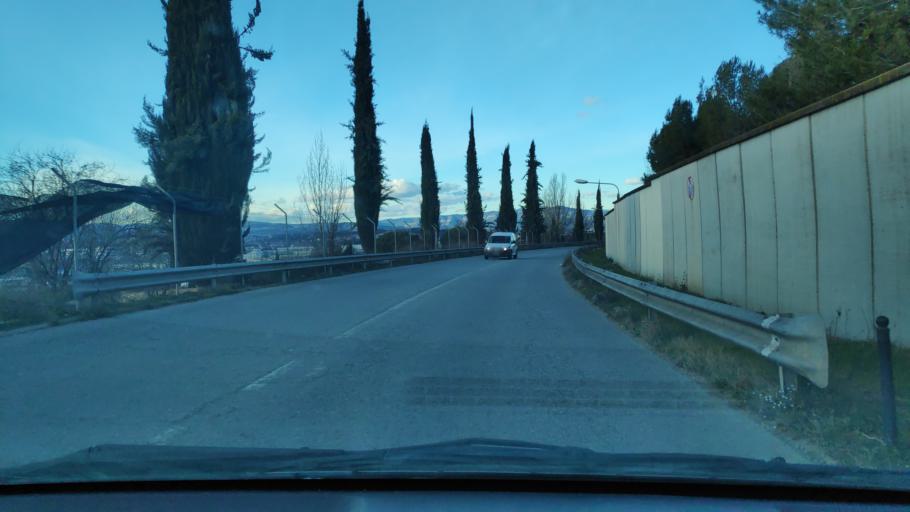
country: ES
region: Catalonia
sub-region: Provincia de Barcelona
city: Montmelo
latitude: 41.5650
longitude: 2.2513
